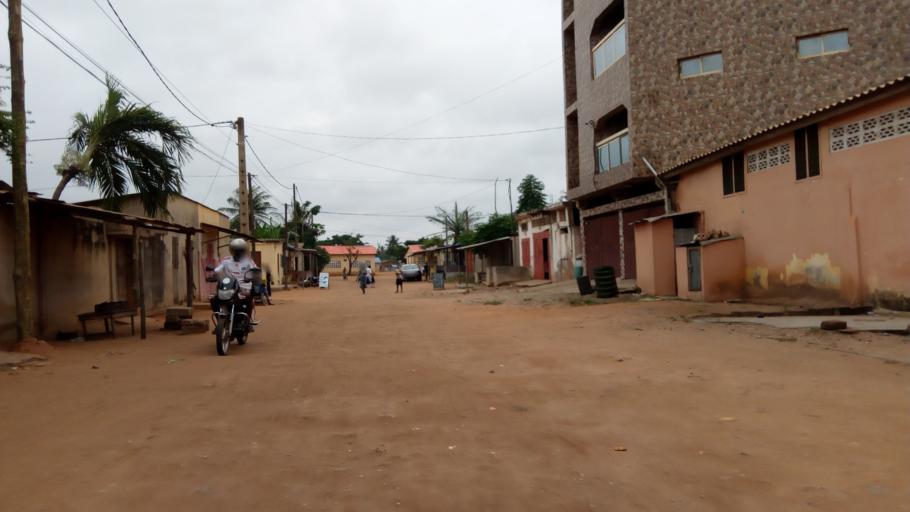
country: TG
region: Maritime
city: Lome
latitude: 6.1778
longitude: 1.1790
